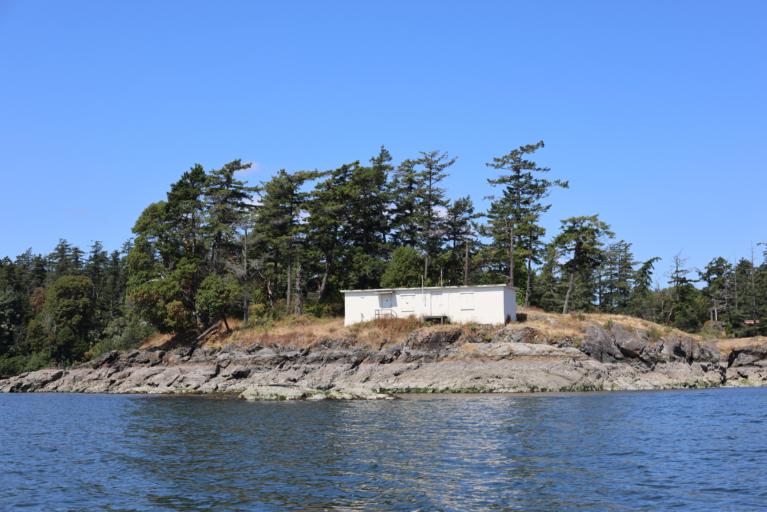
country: CA
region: British Columbia
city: Colwood
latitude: 48.4468
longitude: -123.4470
